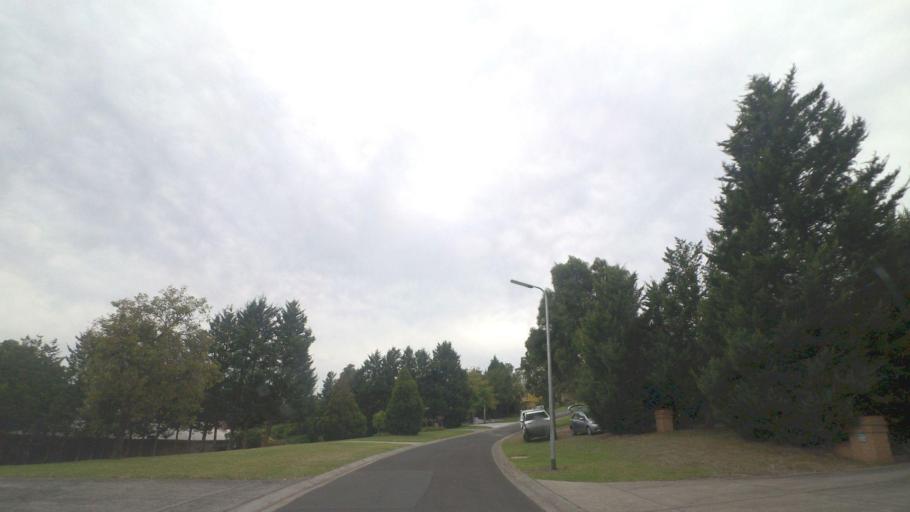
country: AU
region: Victoria
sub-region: Nillumbik
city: Eltham
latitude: -37.7467
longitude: 145.1783
